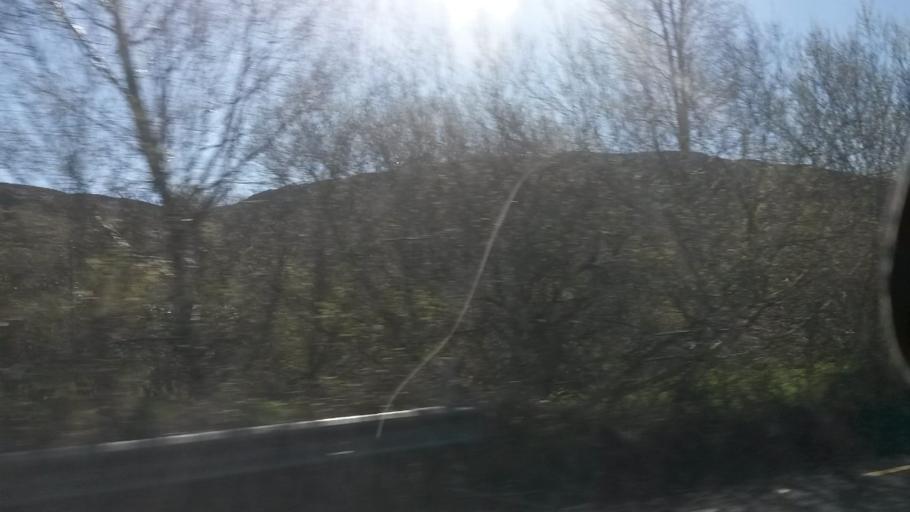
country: IE
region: Munster
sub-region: Ciarrai
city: Cill Airne
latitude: 51.9352
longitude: -9.3825
